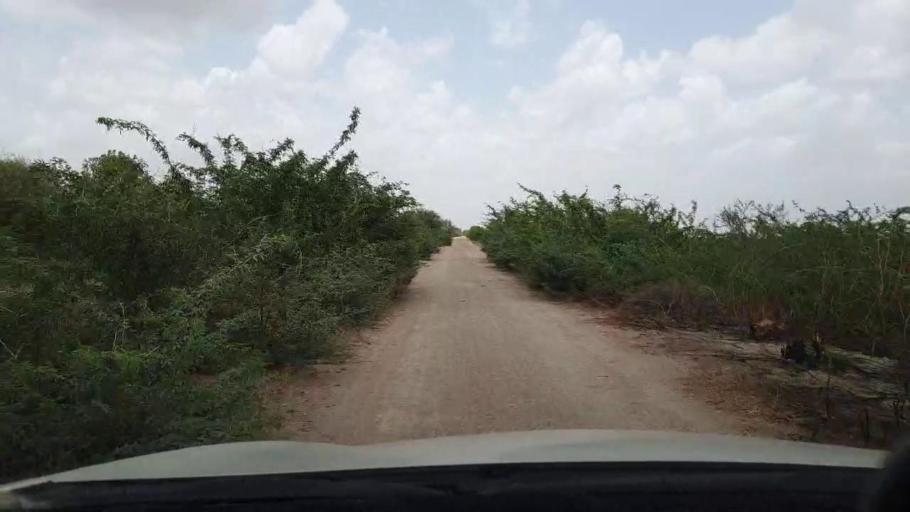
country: PK
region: Sindh
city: Kadhan
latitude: 24.3603
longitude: 68.9536
